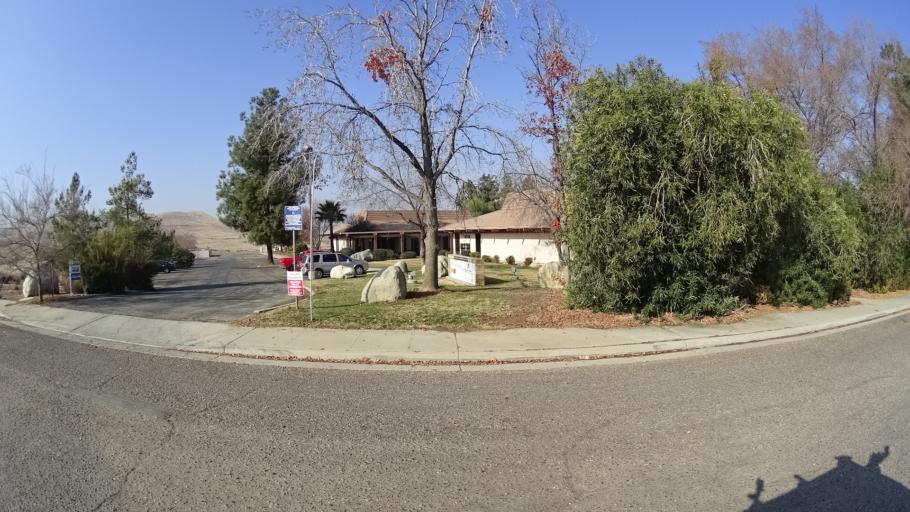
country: US
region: California
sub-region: Kern County
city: Oildale
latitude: 35.4290
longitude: -118.8702
